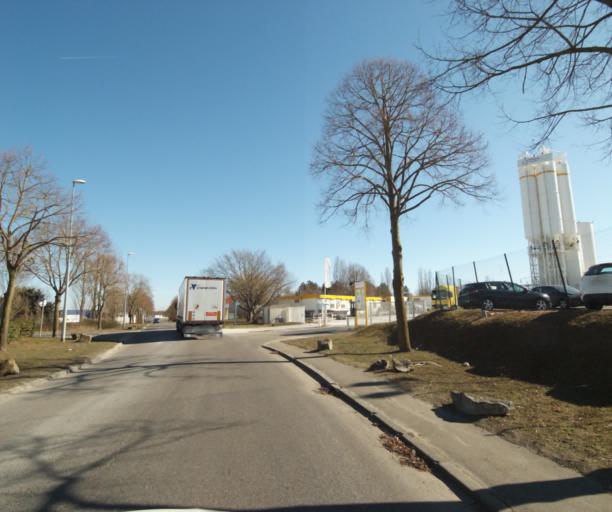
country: FR
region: Lorraine
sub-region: Departement de Meurthe-et-Moselle
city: Fleville-devant-Nancy
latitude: 48.6151
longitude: 6.1903
